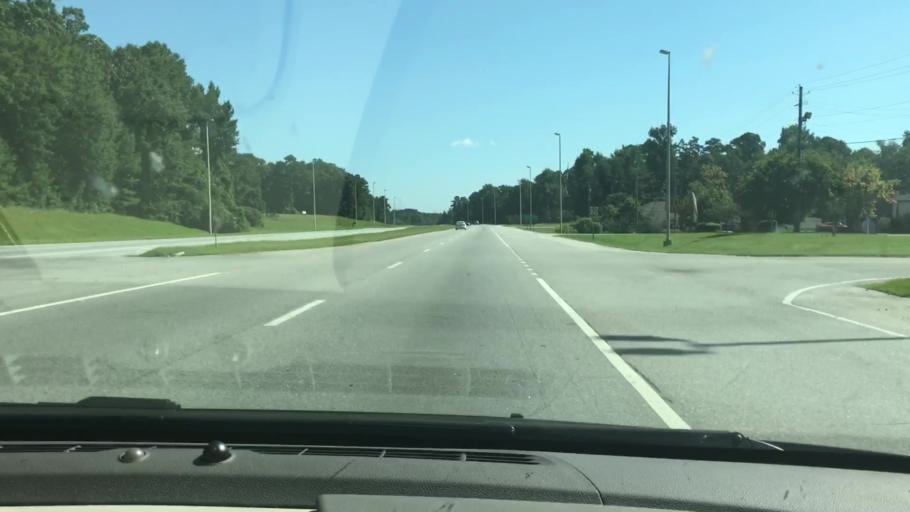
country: US
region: Alabama
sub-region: Russell County
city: Phenix City
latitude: 32.4284
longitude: -85.0329
